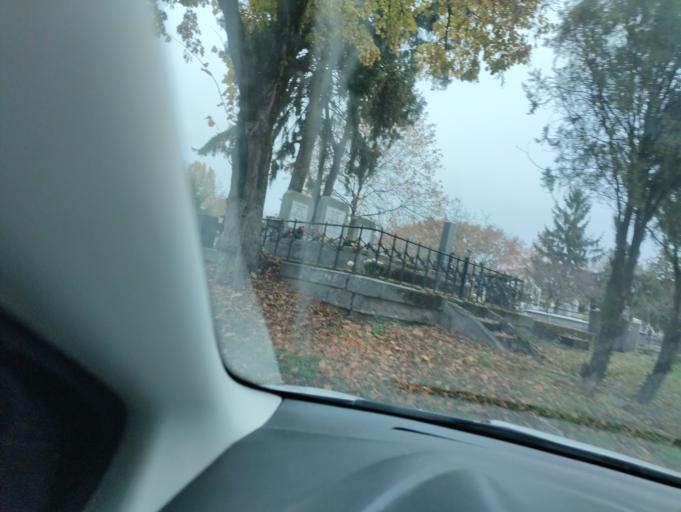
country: RO
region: Bihor
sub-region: Comuna Biharea
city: Oradea
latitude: 47.0412
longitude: 21.9210
